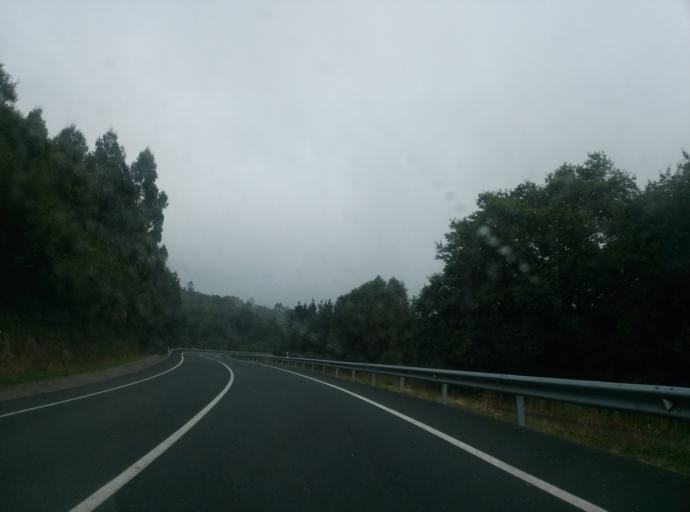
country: ES
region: Galicia
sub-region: Provincia de Lugo
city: Muras
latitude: 43.4315
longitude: -7.7476
